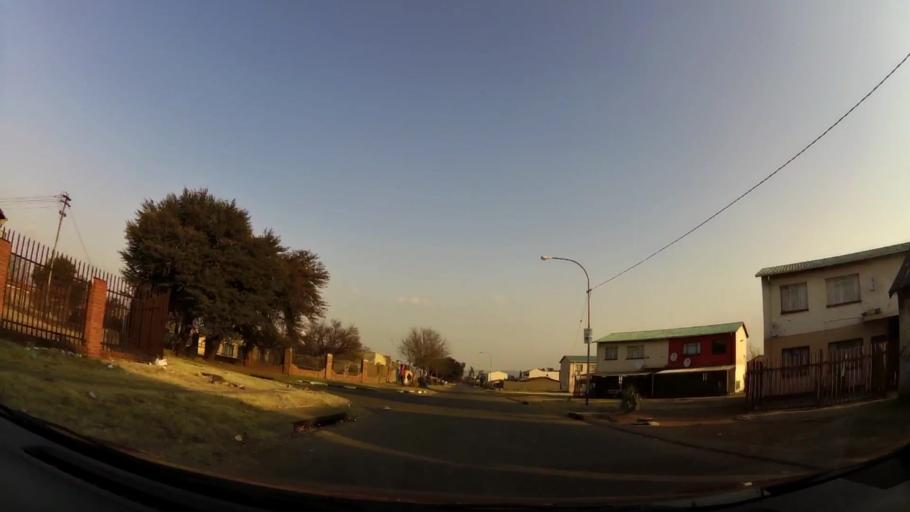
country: ZA
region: Gauteng
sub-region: City of Johannesburg Metropolitan Municipality
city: Soweto
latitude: -26.2845
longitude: 27.8974
